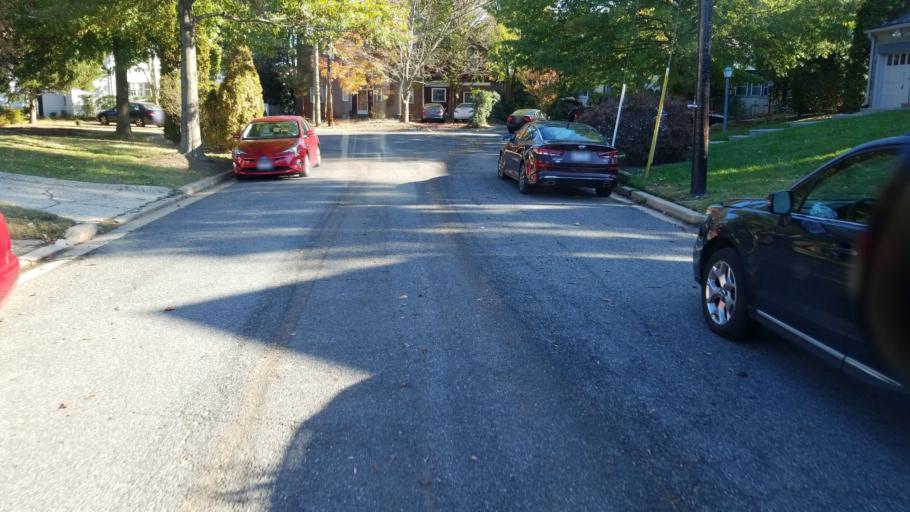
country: US
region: Maryland
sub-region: Montgomery County
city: Chevy Chase
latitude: 38.9659
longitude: -77.0575
